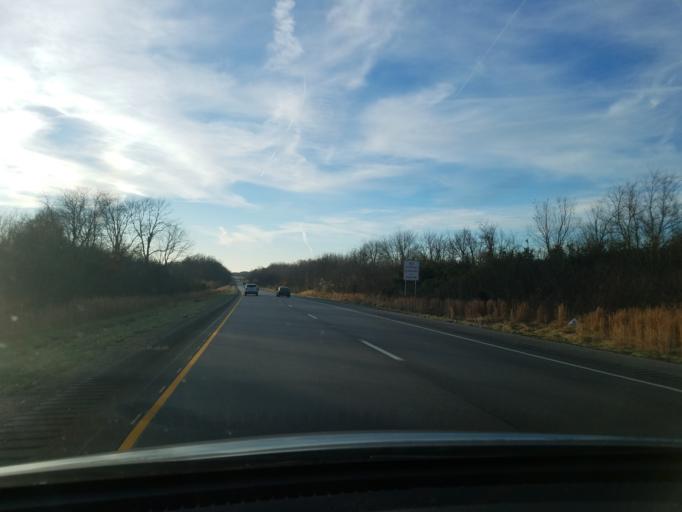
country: US
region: Indiana
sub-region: Spencer County
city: Dale
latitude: 38.1968
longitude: -87.0006
